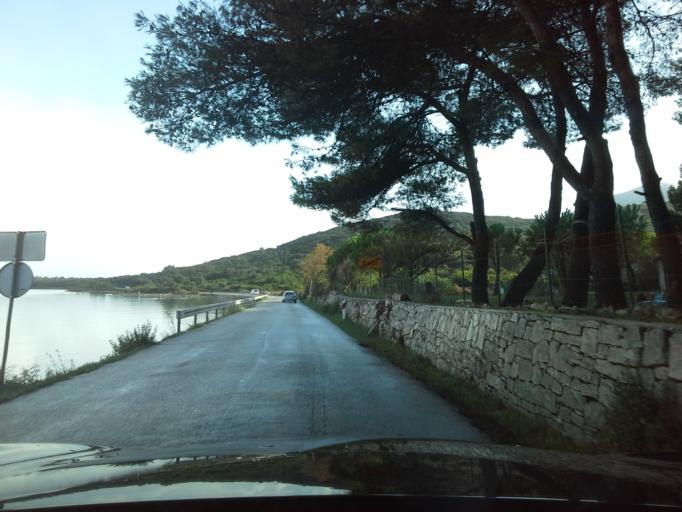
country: HR
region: Primorsko-Goranska
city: Mali Losinj
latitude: 44.6915
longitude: 14.3913
